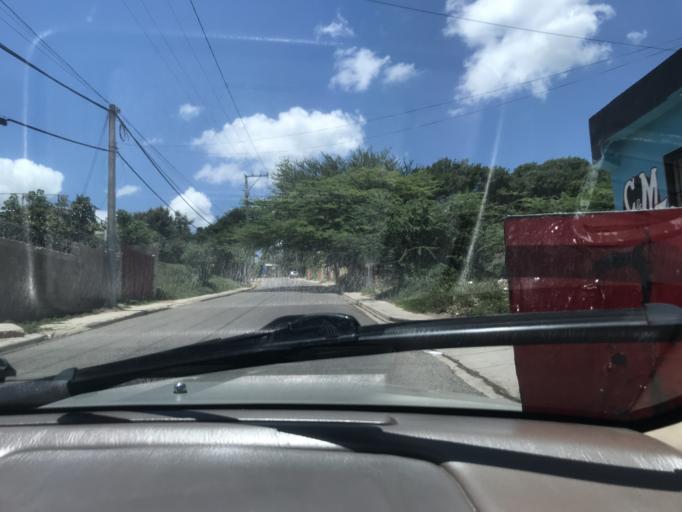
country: DO
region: Santiago
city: Santiago de los Caballeros
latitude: 19.4150
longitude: -70.6862
